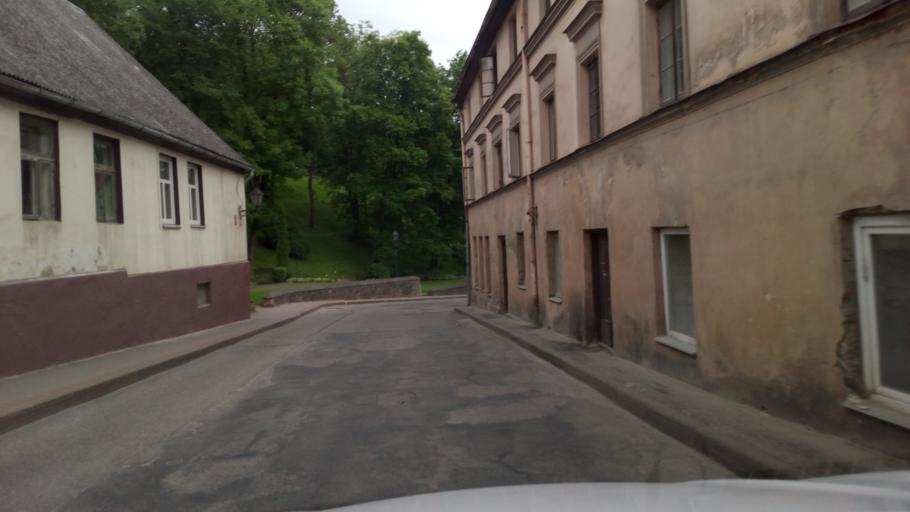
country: LV
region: Kandava
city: Kandava
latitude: 57.0360
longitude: 22.7771
